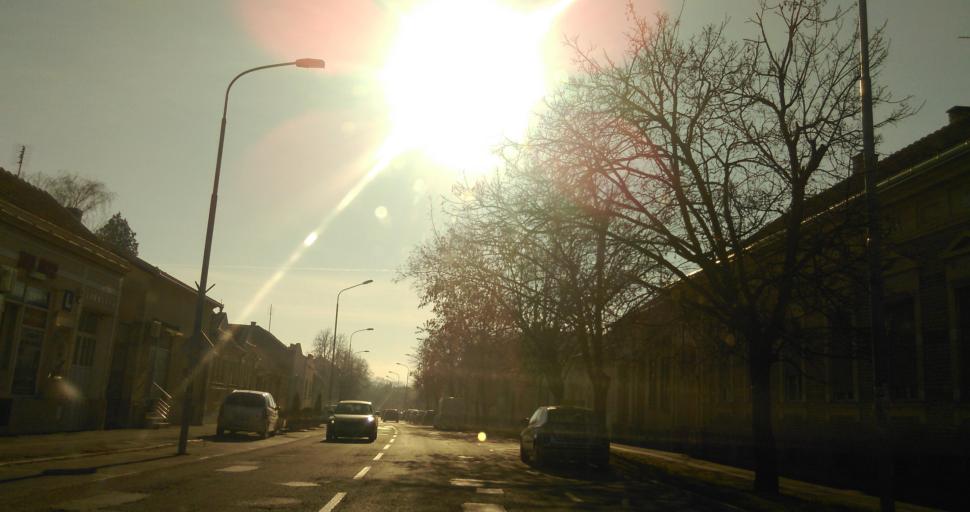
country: RS
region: Autonomna Pokrajina Vojvodina
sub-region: Sremski Okrug
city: Ruma
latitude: 45.0044
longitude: 19.8223
